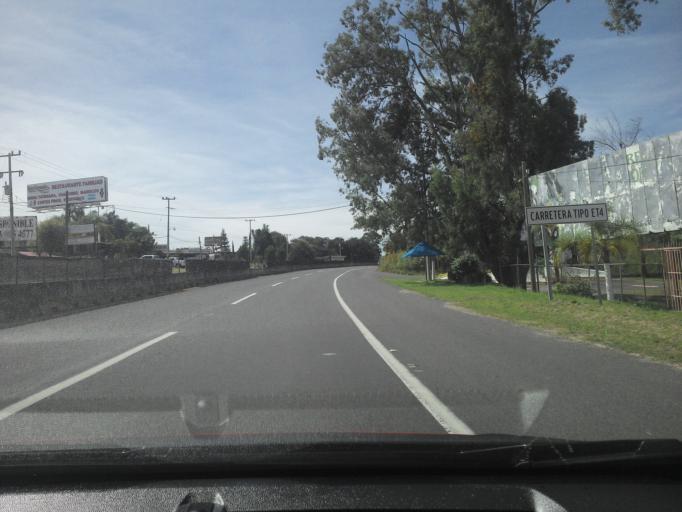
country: MX
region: Jalisco
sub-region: Tala
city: Los Ruisenores
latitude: 20.7222
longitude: -103.6230
